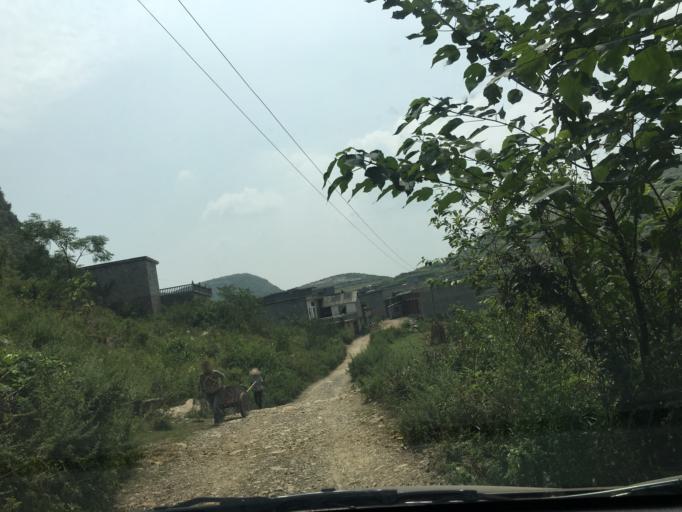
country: CN
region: Guizhou Sheng
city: Anshun
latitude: 25.5979
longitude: 105.6695
